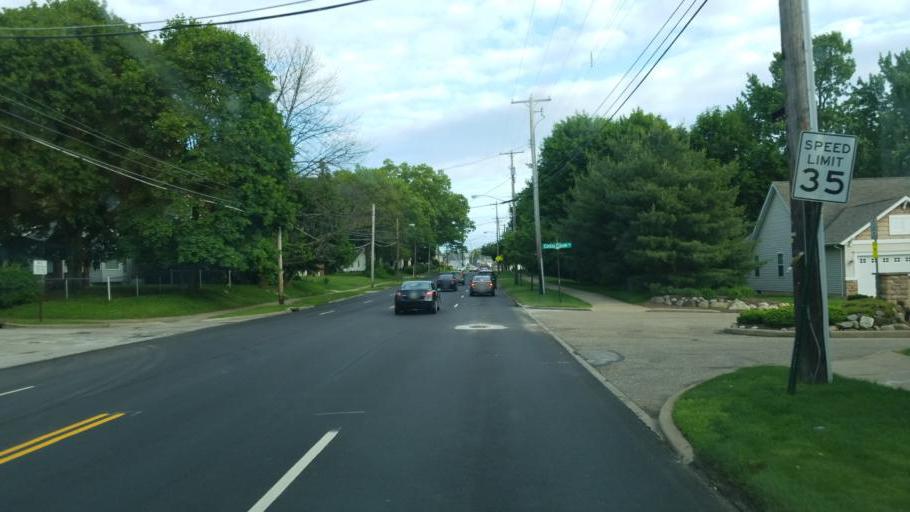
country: US
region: Ohio
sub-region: Summit County
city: Sawyerwood
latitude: 41.0520
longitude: -81.4383
